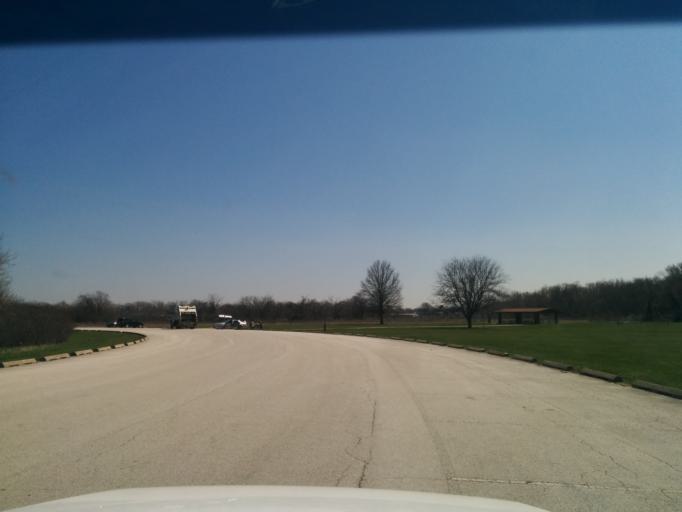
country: US
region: Illinois
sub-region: Cook County
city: Midlothian
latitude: 41.6090
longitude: -87.7237
